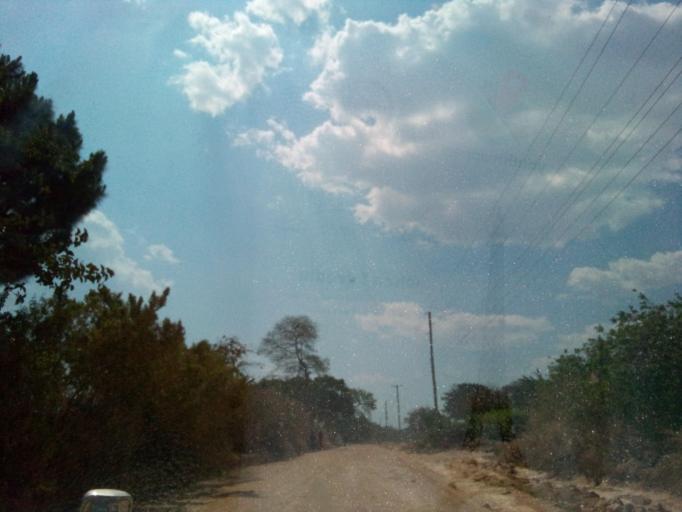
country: ZM
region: Northern
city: Mpika
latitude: -11.8445
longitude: 31.3872
